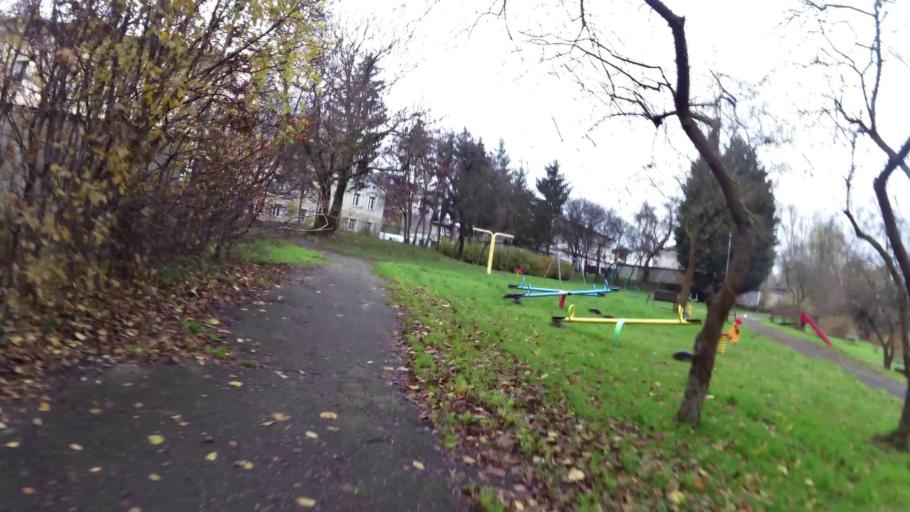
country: PL
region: West Pomeranian Voivodeship
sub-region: Koszalin
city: Koszalin
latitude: 54.1953
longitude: 16.1803
